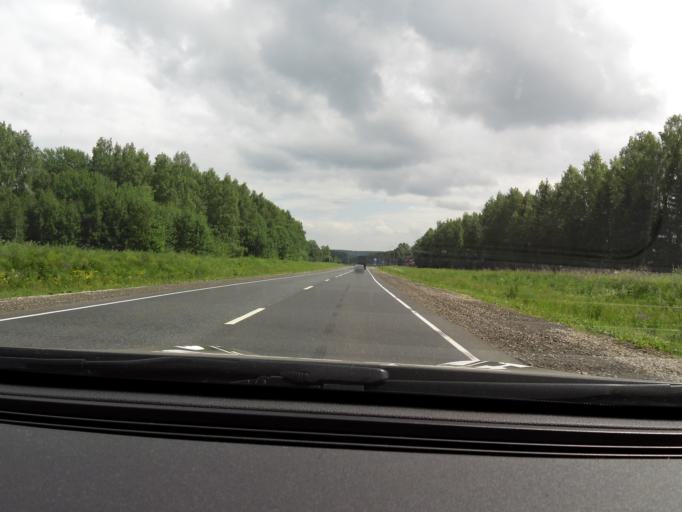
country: RU
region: Perm
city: Suksun
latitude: 57.1535
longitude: 57.2695
